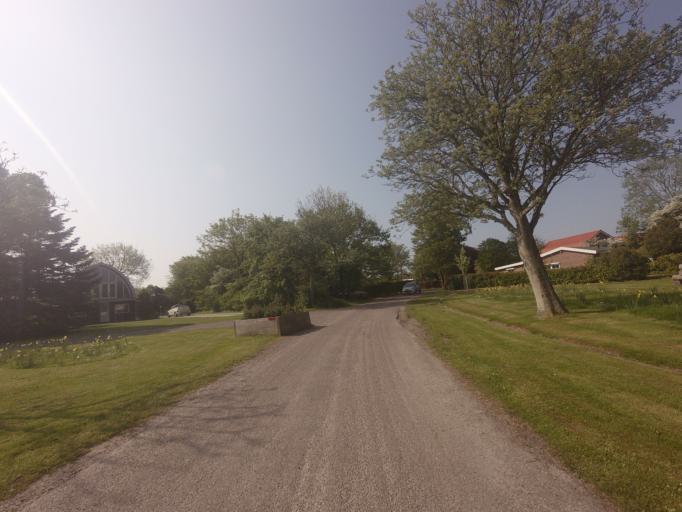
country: NL
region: Zeeland
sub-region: Gemeente Middelburg
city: Middelburg
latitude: 51.5779
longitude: 3.5500
